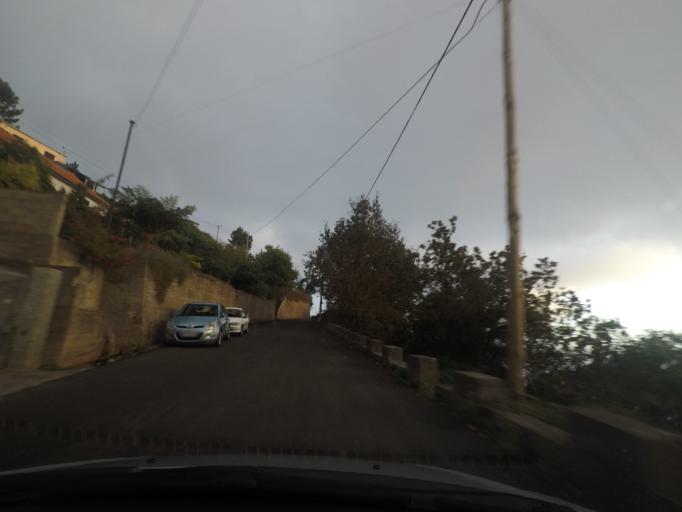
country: PT
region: Madeira
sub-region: Santa Cruz
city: Camacha
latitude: 32.6664
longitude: -16.8479
